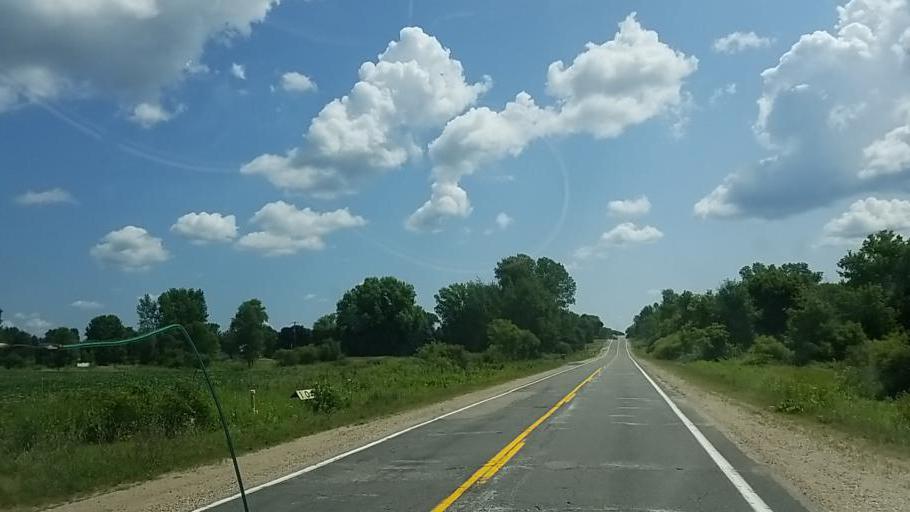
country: US
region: Michigan
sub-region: Kent County
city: Walker
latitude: 43.0740
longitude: -85.7643
